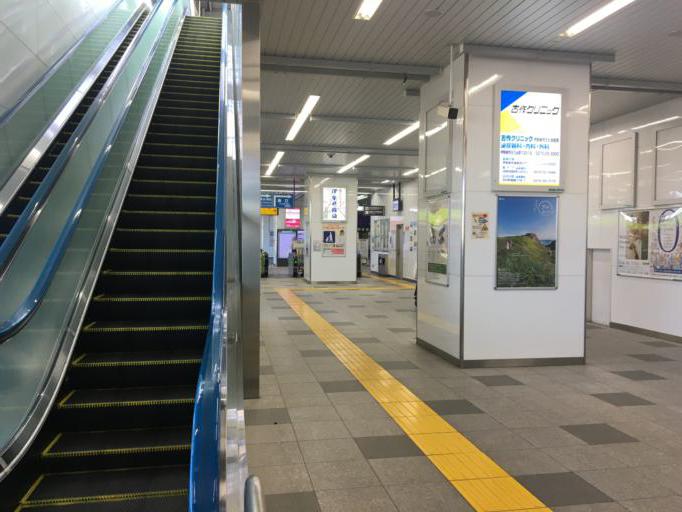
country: JP
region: Gunma
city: Isesaki
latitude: 36.3271
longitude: 139.1941
